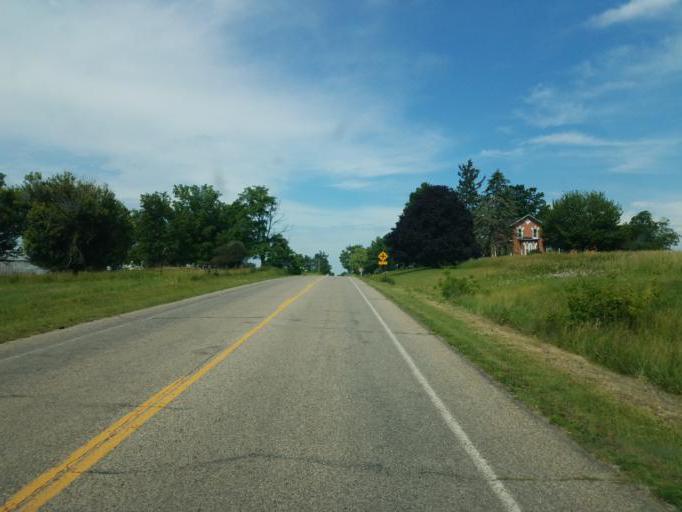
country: US
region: Michigan
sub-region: Barry County
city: Nashville
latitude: 42.6261
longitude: -84.9727
